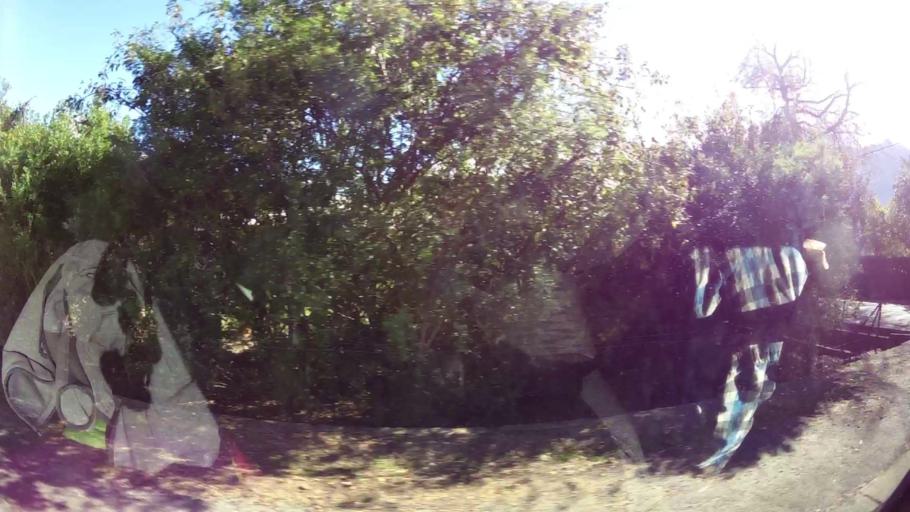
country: ZA
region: Western Cape
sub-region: Overberg District Municipality
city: Swellendam
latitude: -34.0229
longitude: 20.4477
